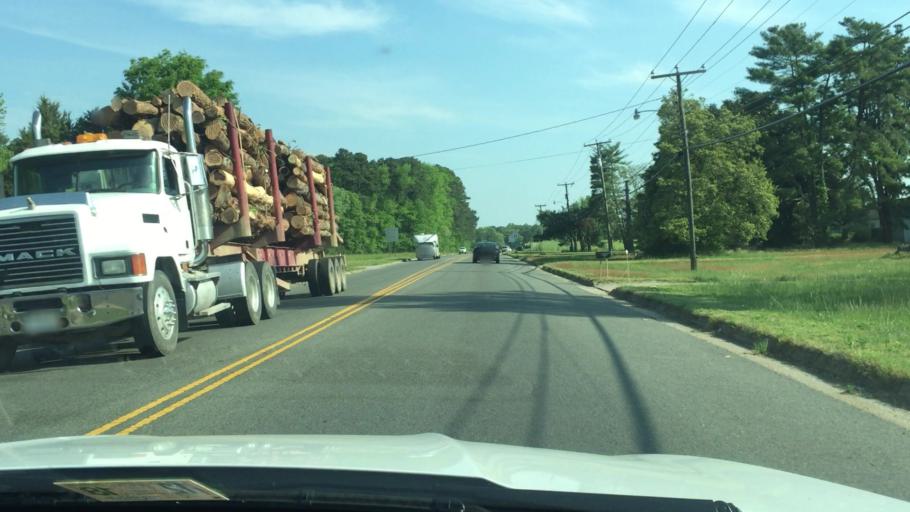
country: US
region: Virginia
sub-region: Lancaster County
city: Kilmarnock
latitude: 37.6507
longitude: -76.3887
